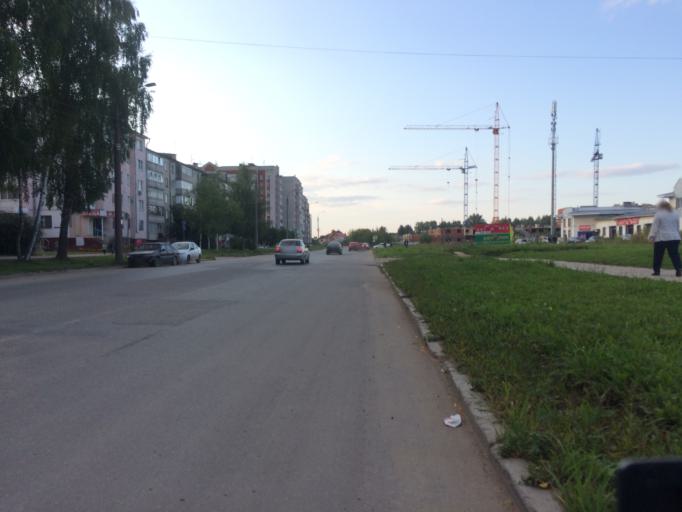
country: RU
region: Mariy-El
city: Medvedevo
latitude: 56.6432
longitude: 47.8449
